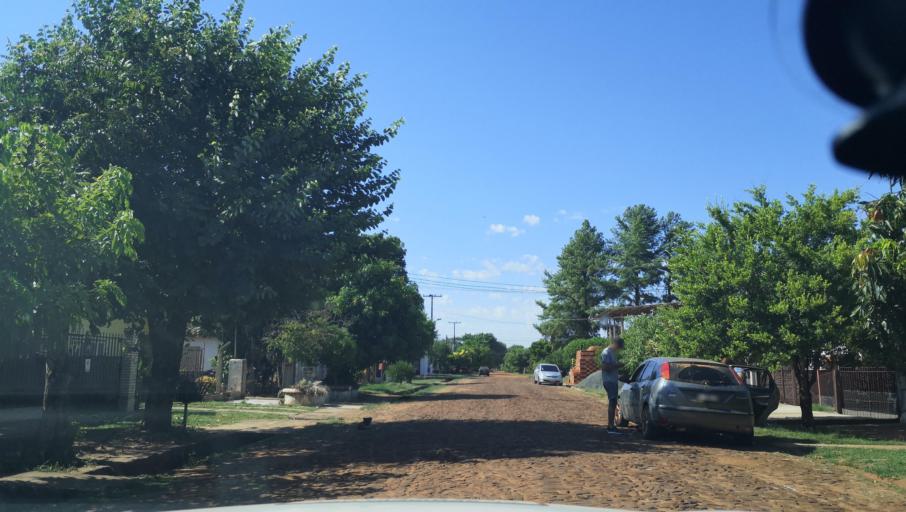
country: PY
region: Itapua
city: Carmen del Parana
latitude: -27.1656
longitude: -56.2349
